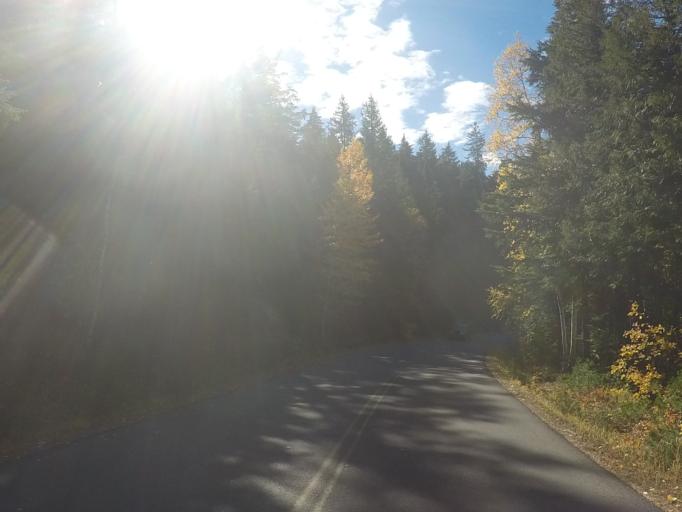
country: US
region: Montana
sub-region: Flathead County
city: Columbia Falls
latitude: 48.5586
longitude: -113.9386
